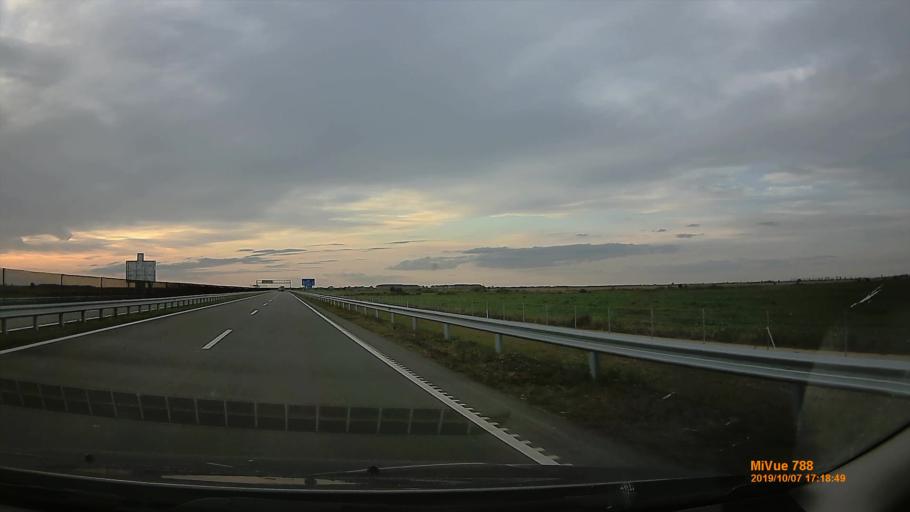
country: HU
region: Jasz-Nagykun-Szolnok
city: Kunszentmarton
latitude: 46.8747
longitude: 20.2584
